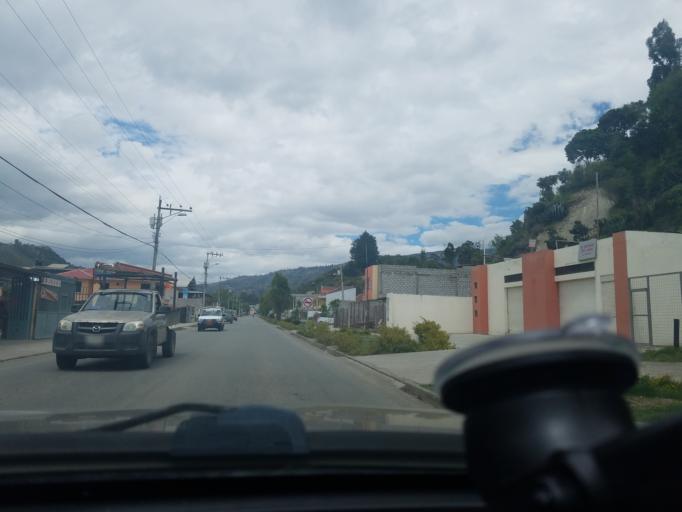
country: EC
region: Azuay
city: La Union
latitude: -2.7913
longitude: -78.7646
